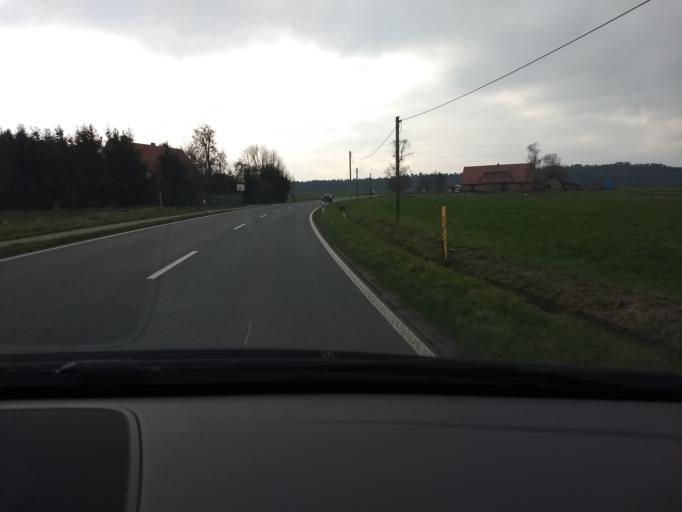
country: DE
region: North Rhine-Westphalia
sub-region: Regierungsbezirk Munster
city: Heiden
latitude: 51.8698
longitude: 6.9198
